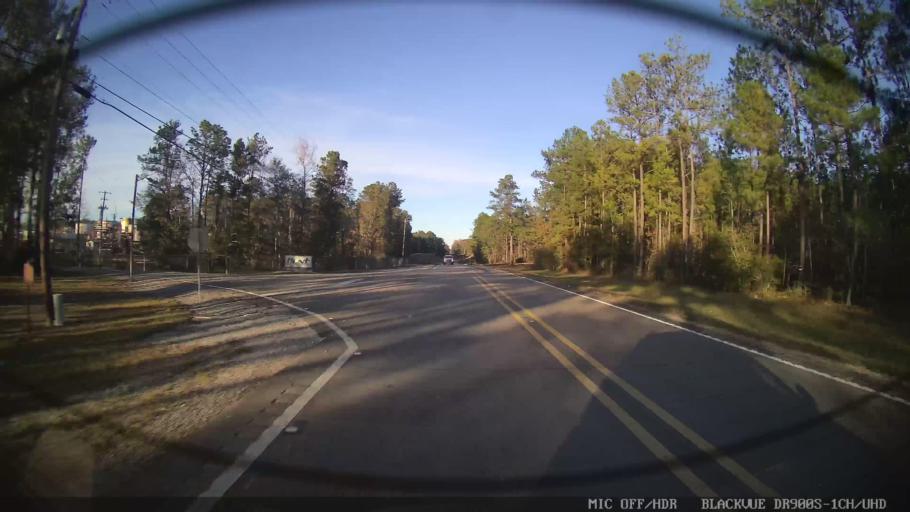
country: US
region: Mississippi
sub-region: Lamar County
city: Lumberton
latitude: 31.0247
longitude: -89.4480
